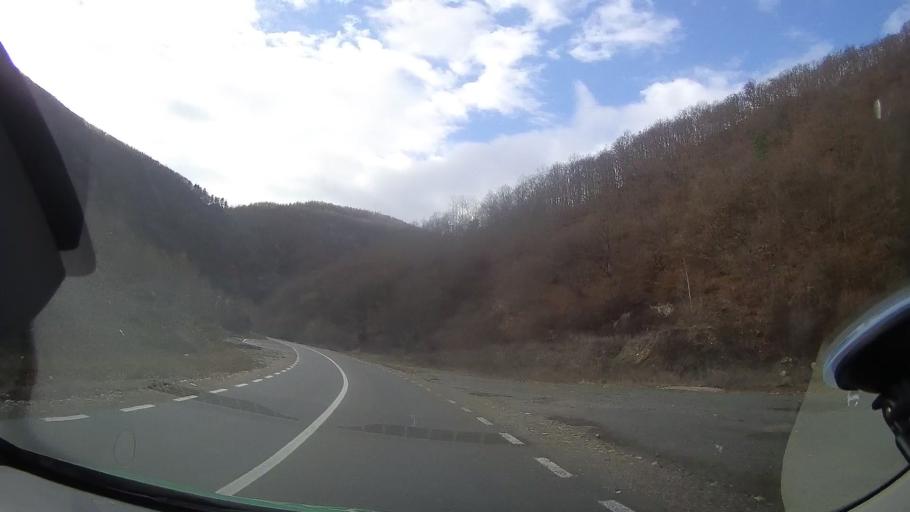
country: RO
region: Cluj
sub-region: Comuna Baisoara
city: Baisoara
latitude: 46.5877
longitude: 23.4458
